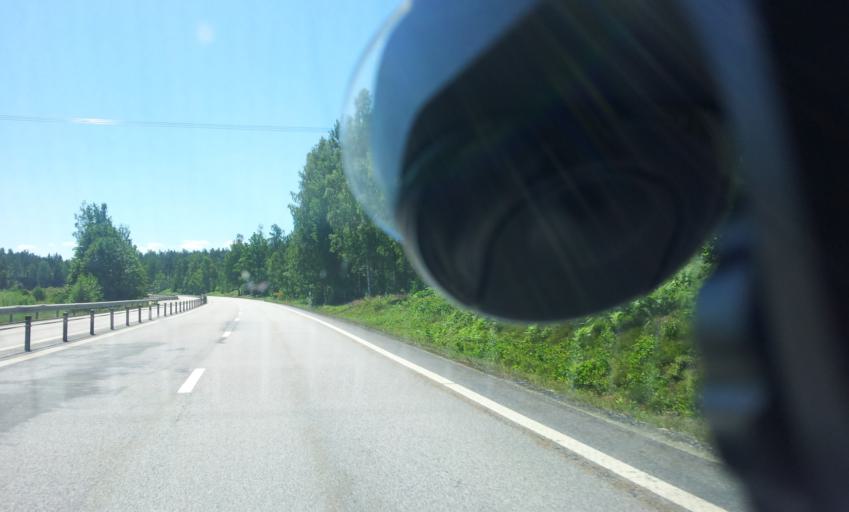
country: SE
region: Kalmar
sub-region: Vasterviks Kommun
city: Forserum
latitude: 58.0530
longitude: 16.5263
